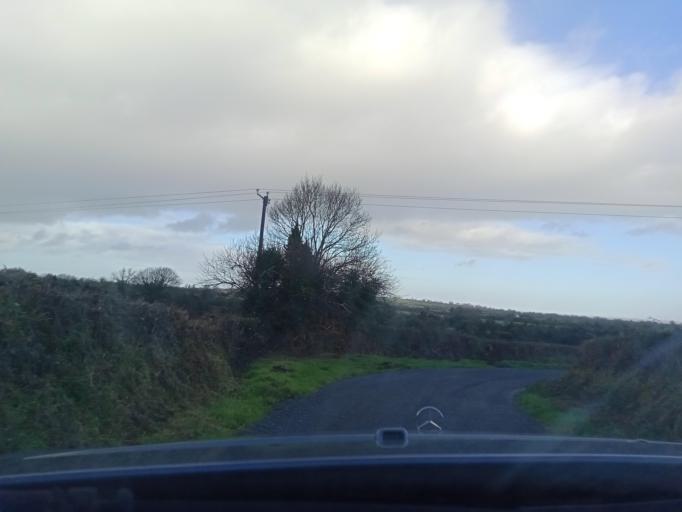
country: IE
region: Leinster
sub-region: Kilkenny
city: Callan
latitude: 52.4675
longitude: -7.3947
